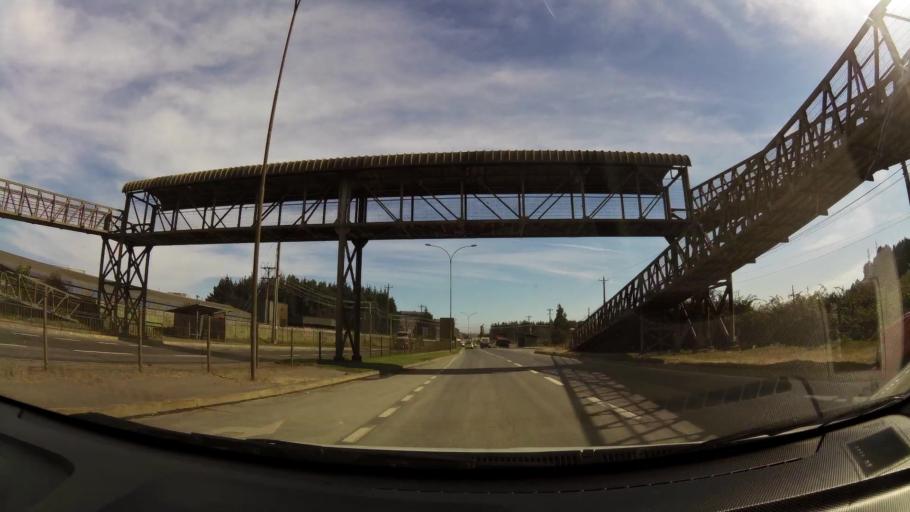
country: CL
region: Biobio
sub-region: Provincia de Concepcion
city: Talcahuano
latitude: -36.7551
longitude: -73.1230
